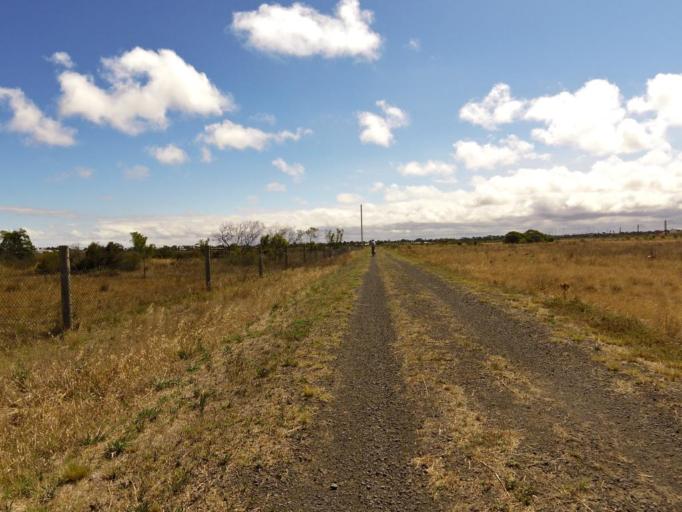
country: AU
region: Victoria
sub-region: Hobsons Bay
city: Altona Meadows
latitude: -37.8645
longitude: 144.8030
